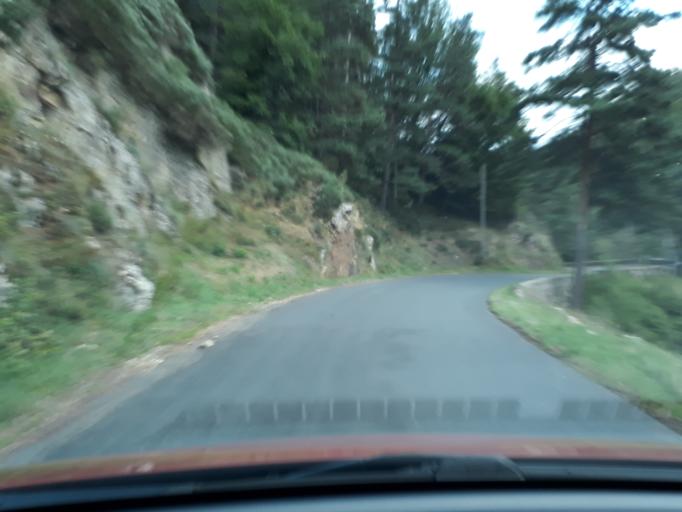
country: FR
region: Auvergne
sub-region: Departement de la Haute-Loire
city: Le Monastier-sur-Gazeille
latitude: 44.8240
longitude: 3.9441
